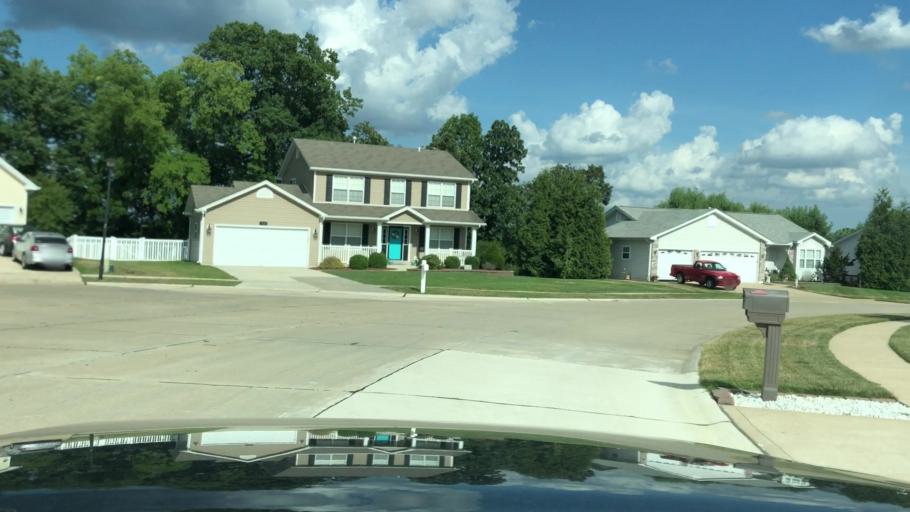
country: US
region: Missouri
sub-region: Saint Charles County
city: Wentzville
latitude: 38.8390
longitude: -90.8838
